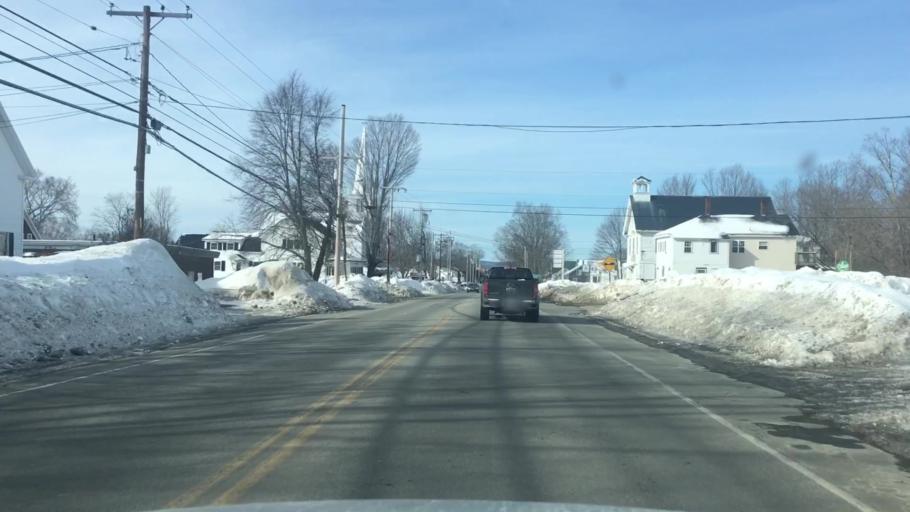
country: US
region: Maine
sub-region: Penobscot County
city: Charleston
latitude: 45.0010
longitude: -69.0222
